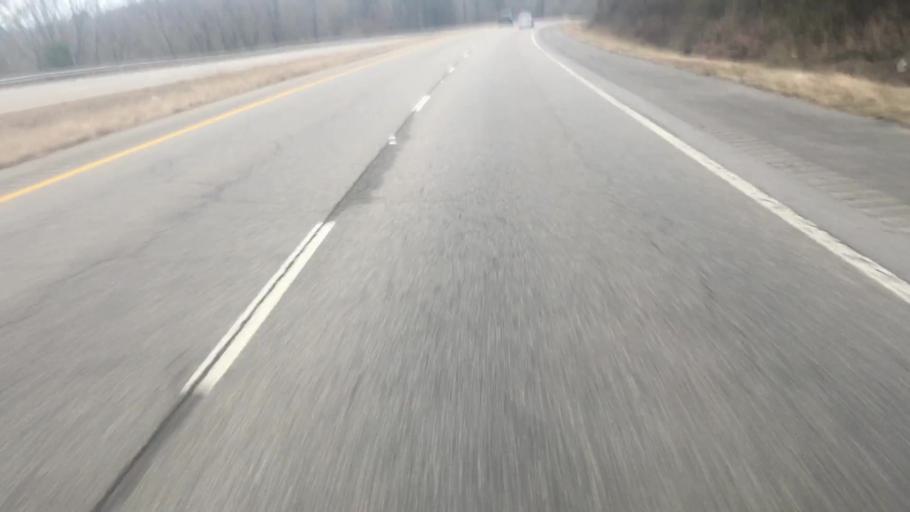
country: US
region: Alabama
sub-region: Walker County
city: Cordova
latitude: 33.8154
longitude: -87.1490
